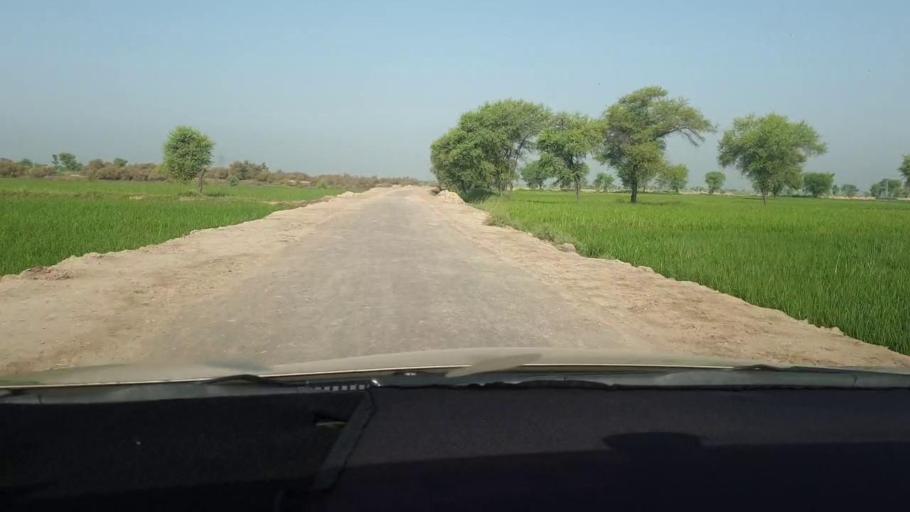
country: PK
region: Sindh
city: Miro Khan
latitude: 27.7550
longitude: 68.1476
